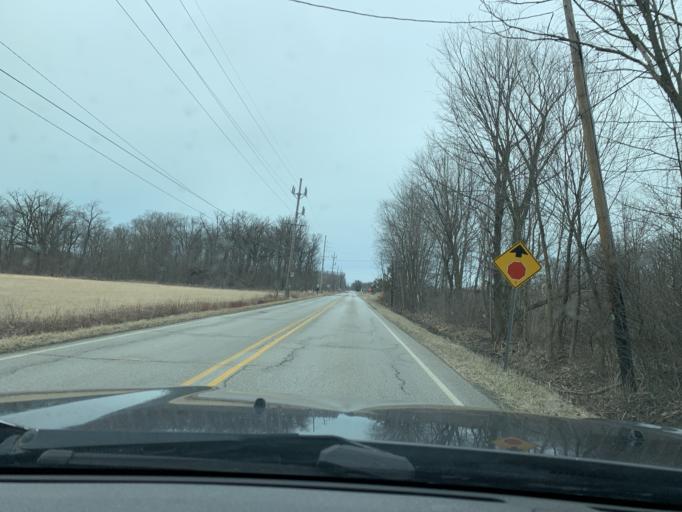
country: US
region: Indiana
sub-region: Porter County
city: Chesterton
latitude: 41.5850
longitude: -87.0667
